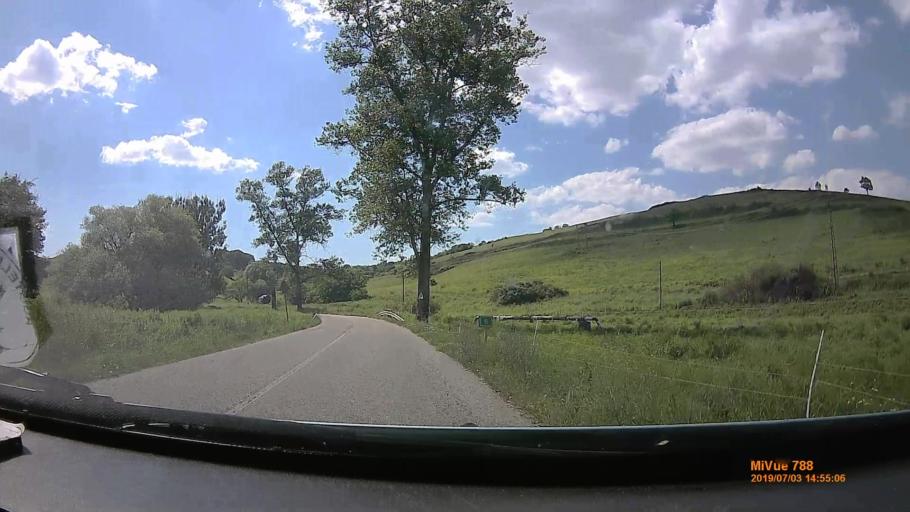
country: HU
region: Borsod-Abauj-Zemplen
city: Putnok
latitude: 48.2645
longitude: 20.4073
